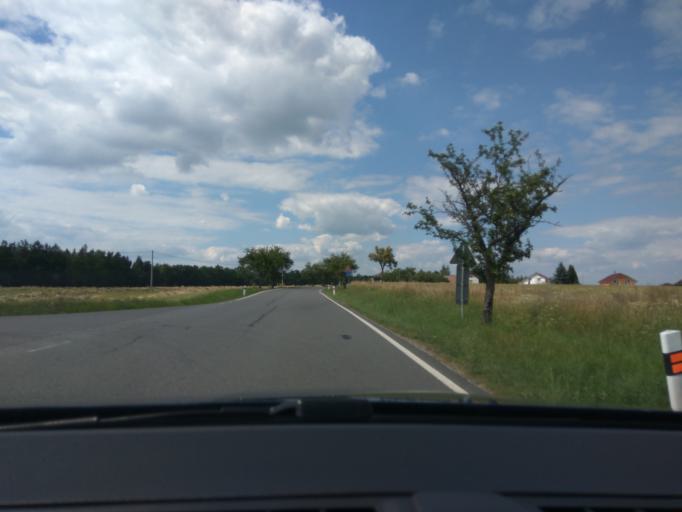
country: CZ
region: Jihocesky
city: Milevsko
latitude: 49.4115
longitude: 14.3592
